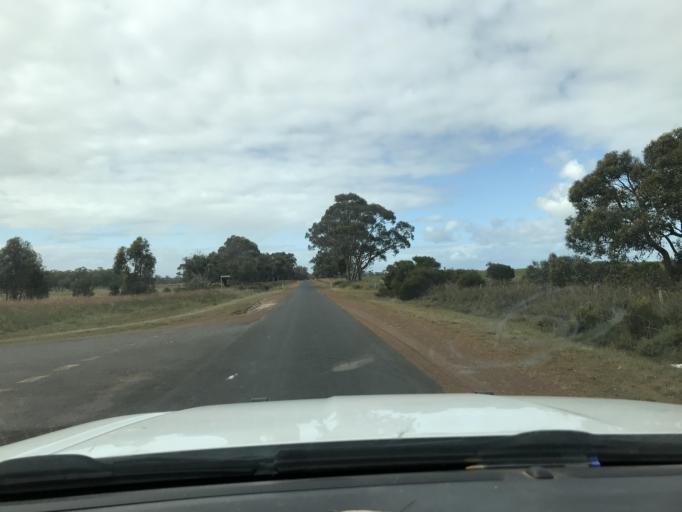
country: AU
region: South Australia
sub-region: Wattle Range
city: Penola
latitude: -37.0981
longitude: 141.2784
